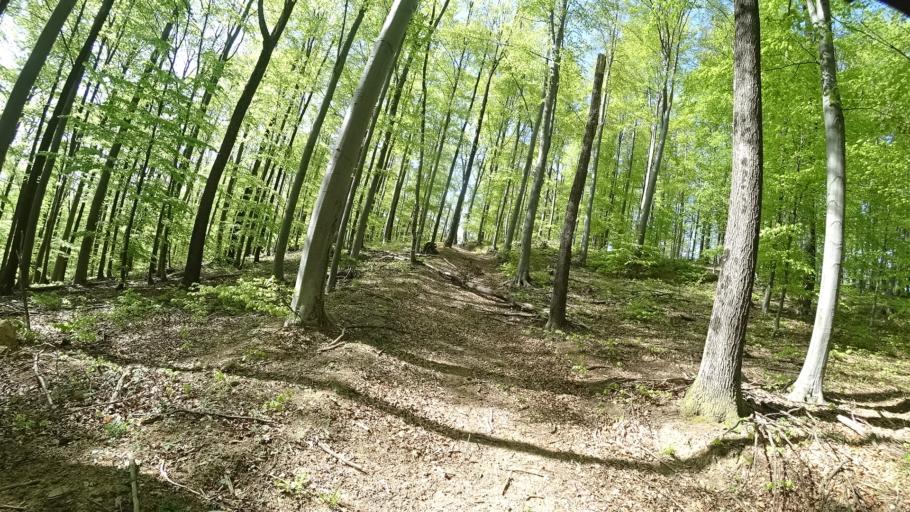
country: HR
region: Zagrebacka
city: Jablanovec
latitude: 45.8967
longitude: 15.9073
